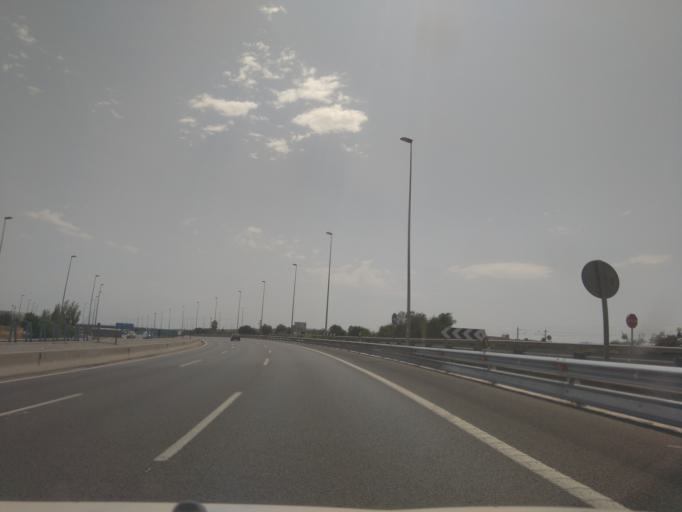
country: ES
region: Valencia
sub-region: Provincia de Valencia
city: Silla
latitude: 39.3716
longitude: -0.4261
